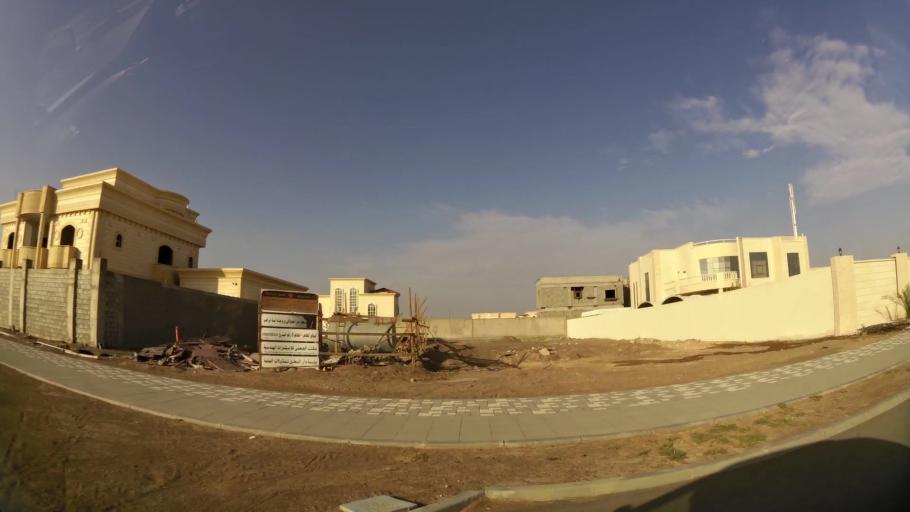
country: AE
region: Abu Dhabi
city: Al Ain
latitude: 24.0968
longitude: 55.8510
